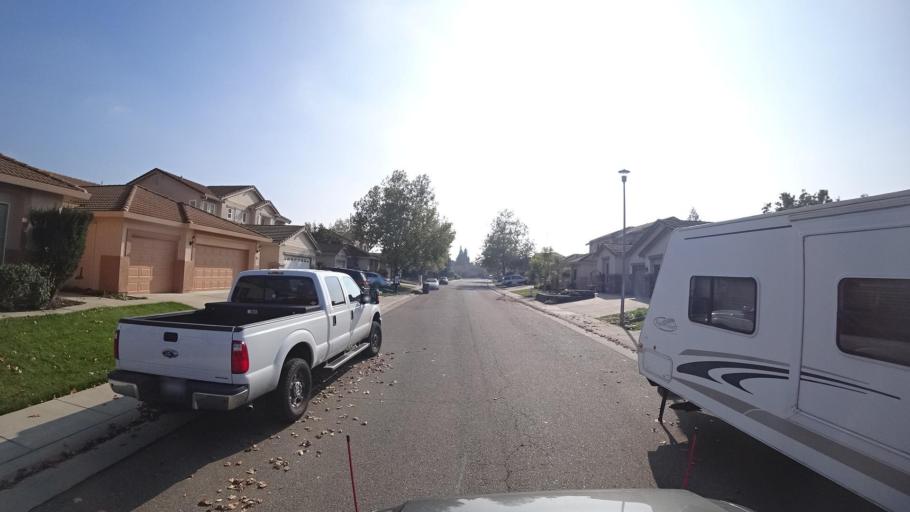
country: US
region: California
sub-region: Sacramento County
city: Elk Grove
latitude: 38.4202
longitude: -121.3420
